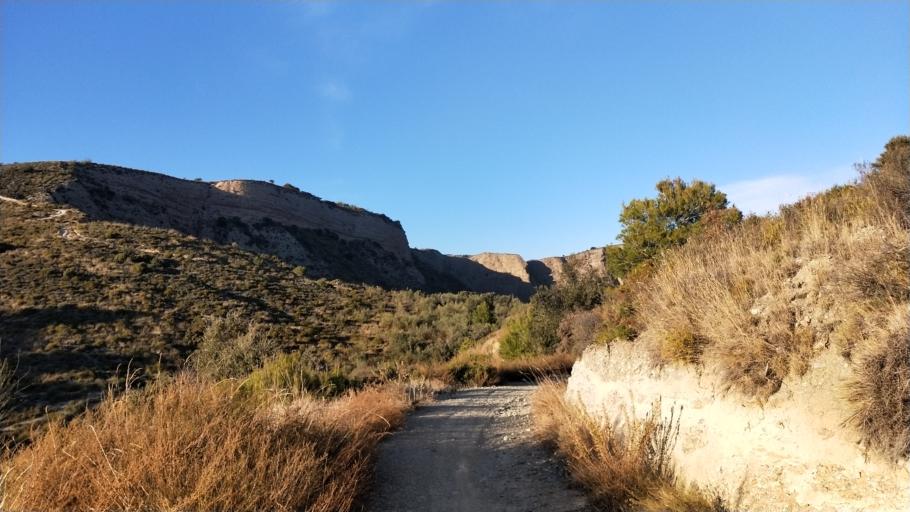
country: ES
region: Andalusia
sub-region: Provincia de Granada
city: Dudar
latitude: 37.1951
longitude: -3.5011
